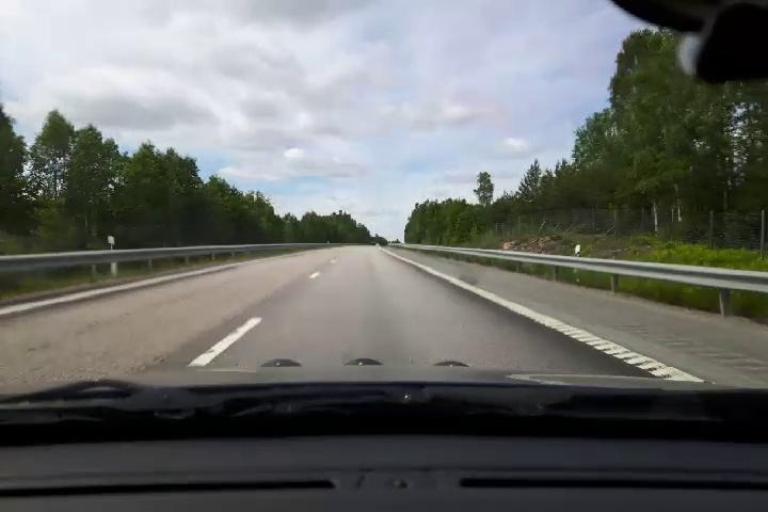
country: SE
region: Uppsala
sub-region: Alvkarleby Kommun
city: AElvkarleby
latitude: 60.4774
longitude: 17.3736
